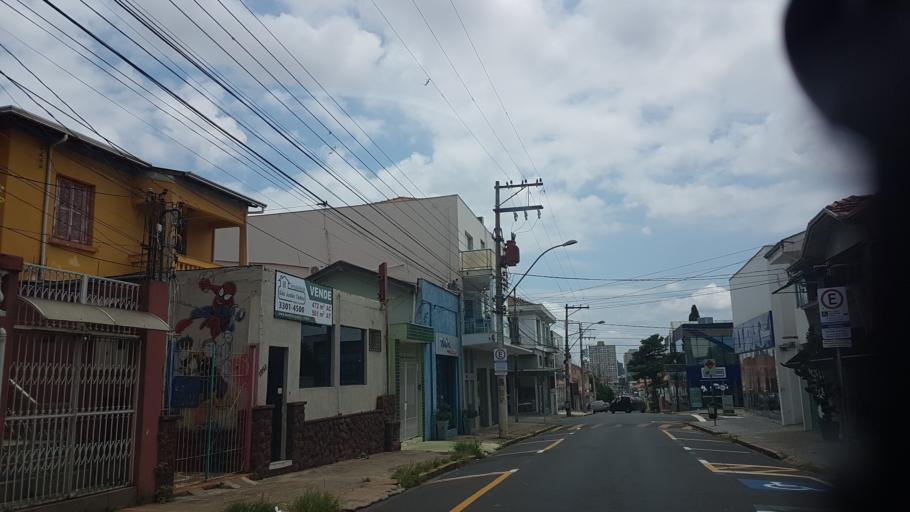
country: BR
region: Sao Paulo
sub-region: Piracicaba
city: Piracicaba
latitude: -22.7341
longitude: -47.6520
